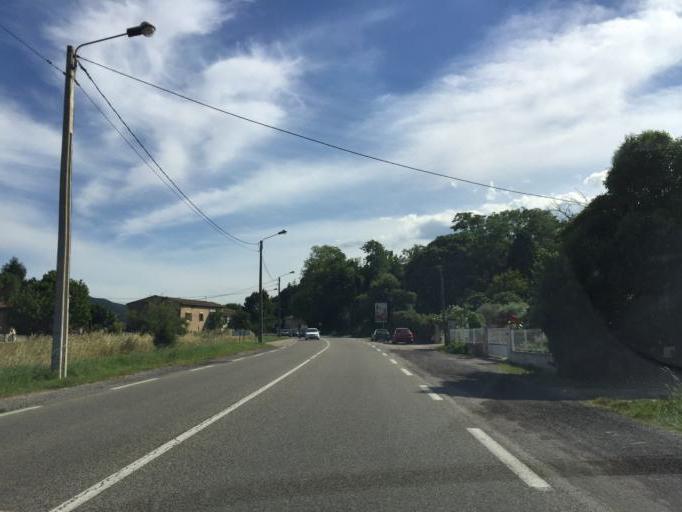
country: FR
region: Rhone-Alpes
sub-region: Departement de l'Ardeche
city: Le Pouzin
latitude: 44.7409
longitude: 4.7426
